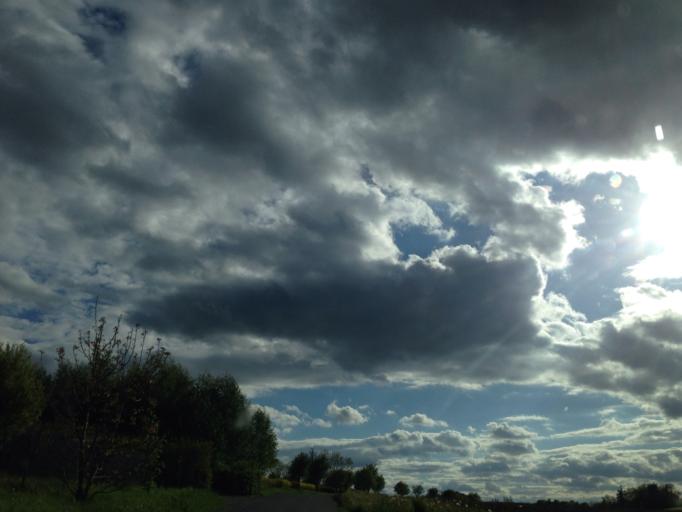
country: DE
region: Thuringia
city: Wernburg
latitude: 50.6716
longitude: 11.5892
